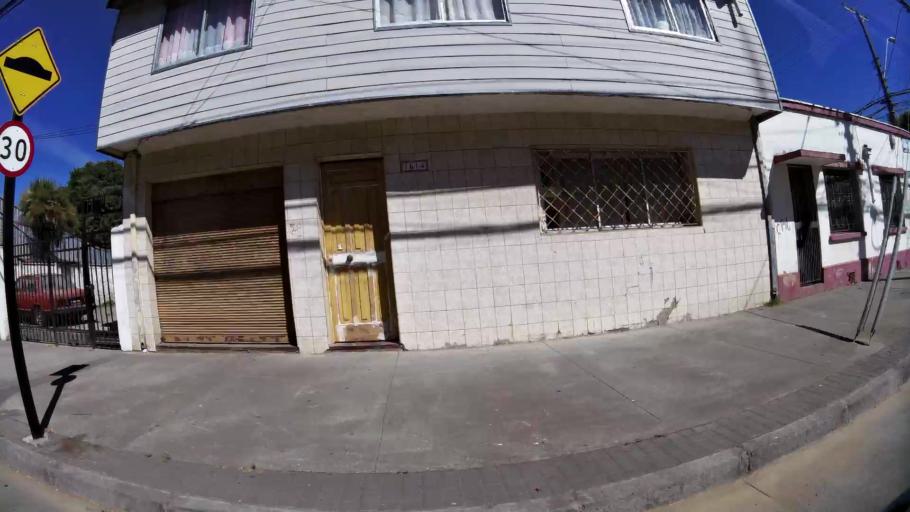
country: CL
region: Biobio
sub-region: Provincia de Concepcion
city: Concepcion
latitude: -36.8164
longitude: -73.0415
